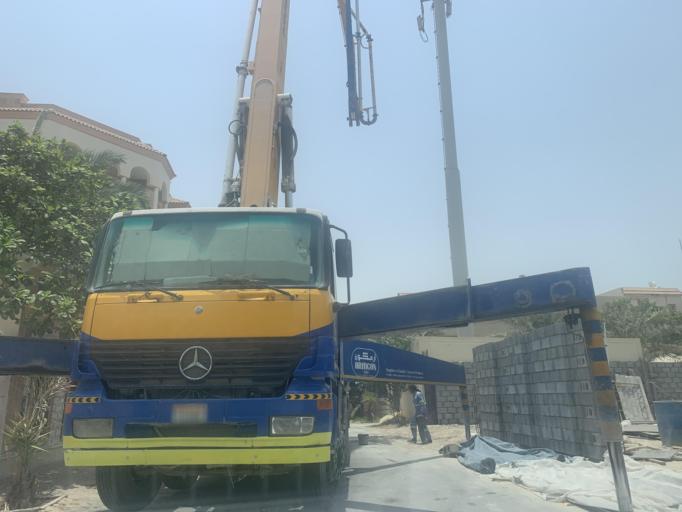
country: BH
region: Manama
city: Jidd Hafs
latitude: 26.2212
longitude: 50.4581
